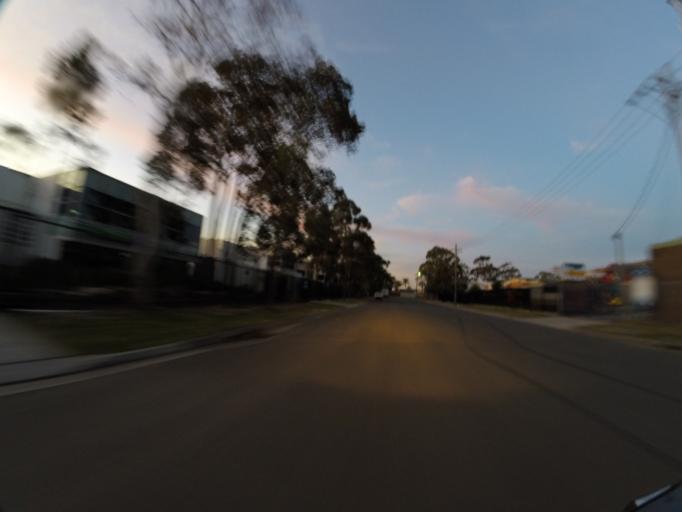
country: AU
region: New South Wales
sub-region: Sutherland Shire
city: Heathcote
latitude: -34.0971
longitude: 150.9963
